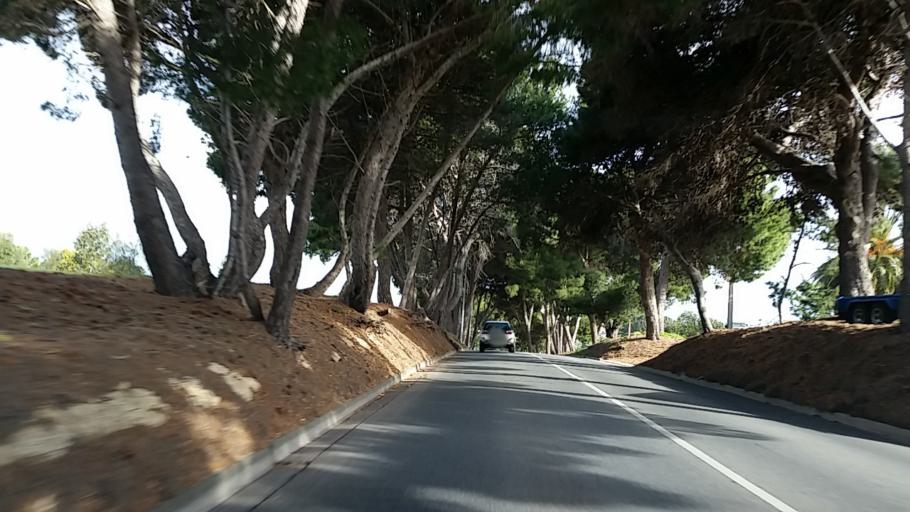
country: AU
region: South Australia
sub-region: Onkaparinga
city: Reynella
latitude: -35.1015
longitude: 138.5346
